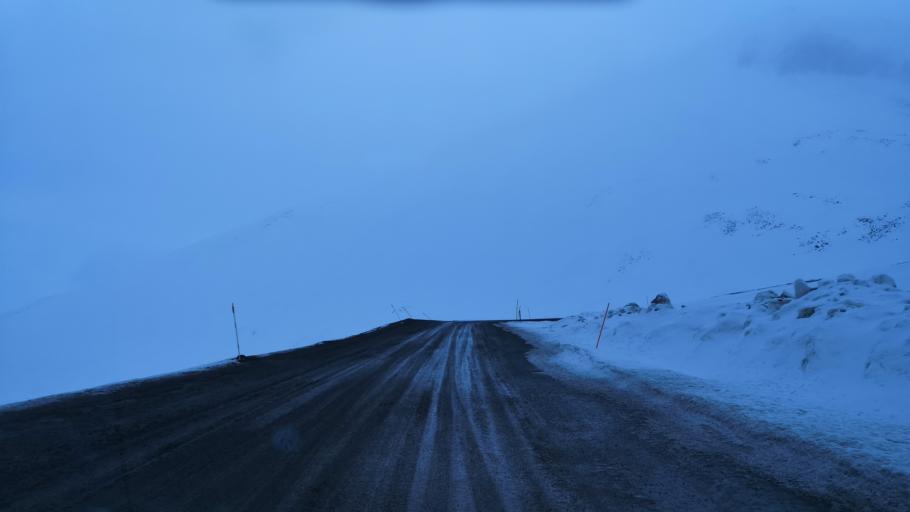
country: SJ
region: Svalbard
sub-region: Spitsbergen
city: Longyearbyen
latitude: 78.2361
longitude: 15.4677
